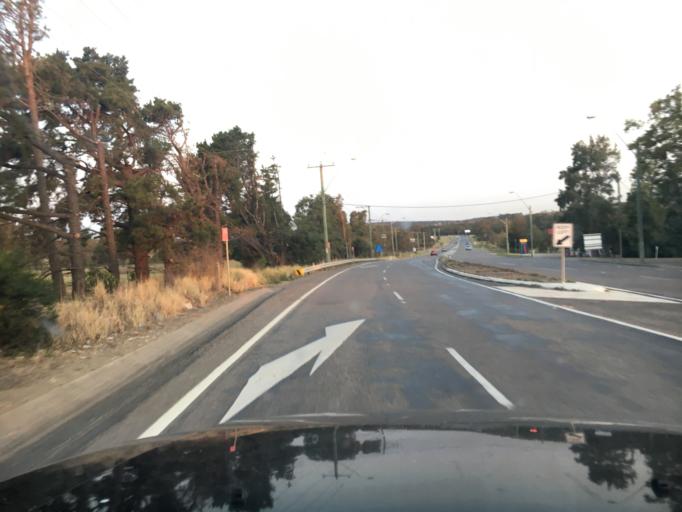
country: AU
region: New South Wales
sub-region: Cessnock
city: Greta
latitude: -32.6656
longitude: 151.3744
